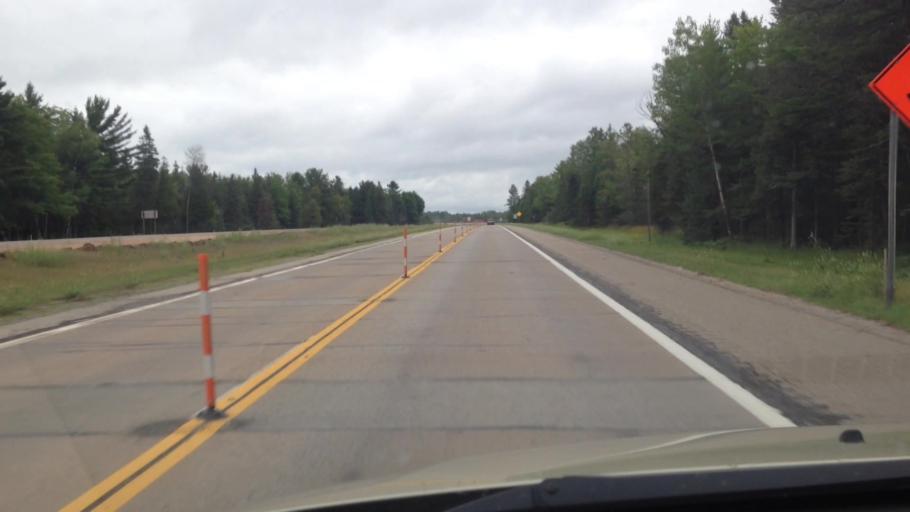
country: US
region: Michigan
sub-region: Delta County
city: Gladstone
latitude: 45.8920
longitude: -87.0018
